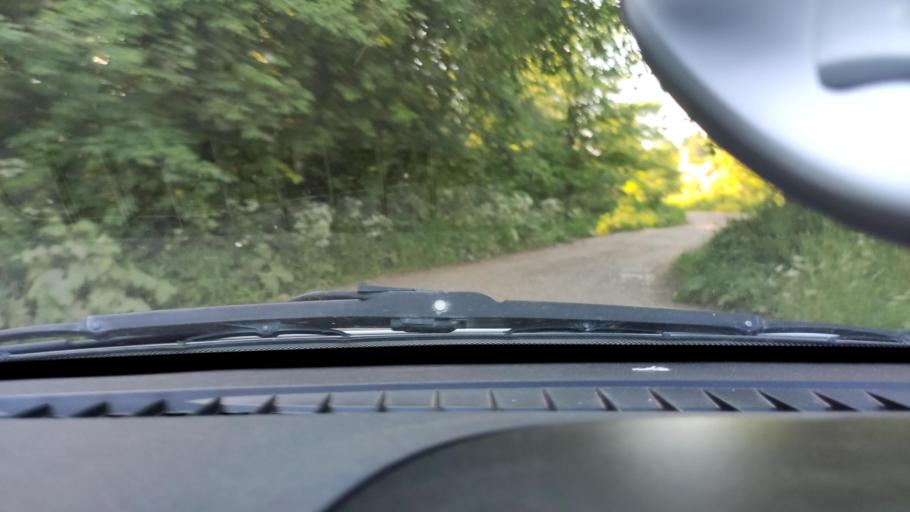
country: RU
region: Perm
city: Bershet'
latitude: 57.6973
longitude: 56.4152
